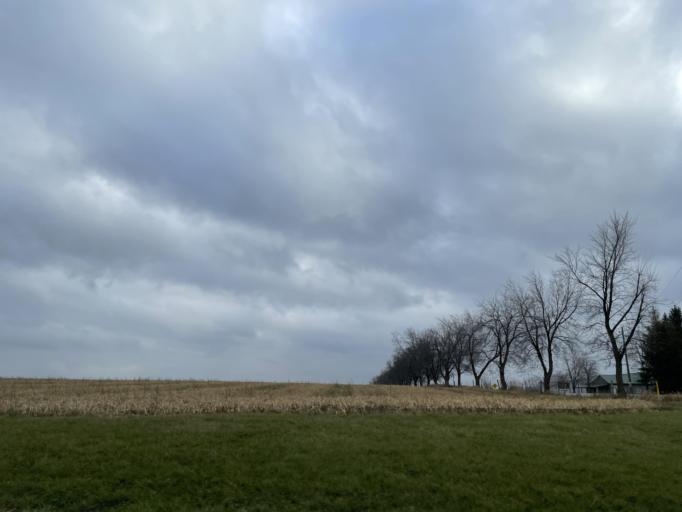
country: CA
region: Ontario
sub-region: Wellington County
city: Guelph
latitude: 43.5187
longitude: -80.3228
